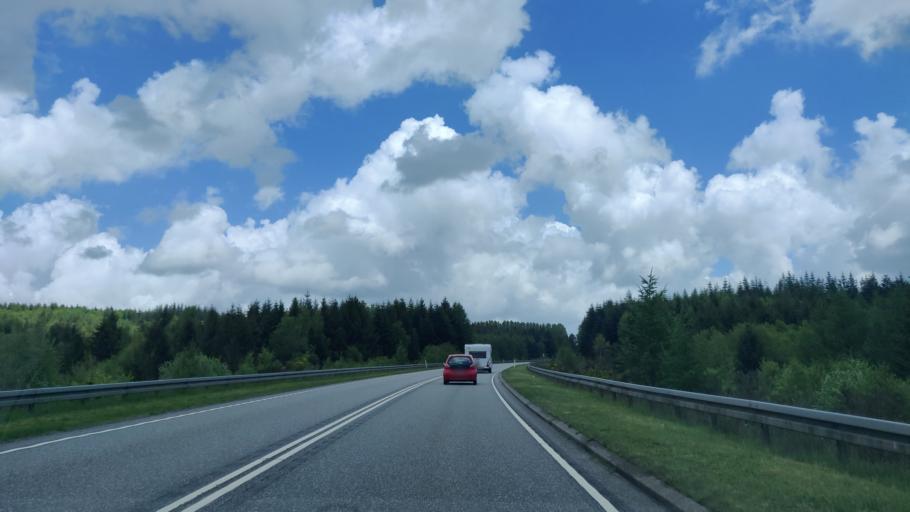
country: DK
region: Central Jutland
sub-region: Hedensted Kommune
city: Torring
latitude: 55.9556
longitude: 9.3982
